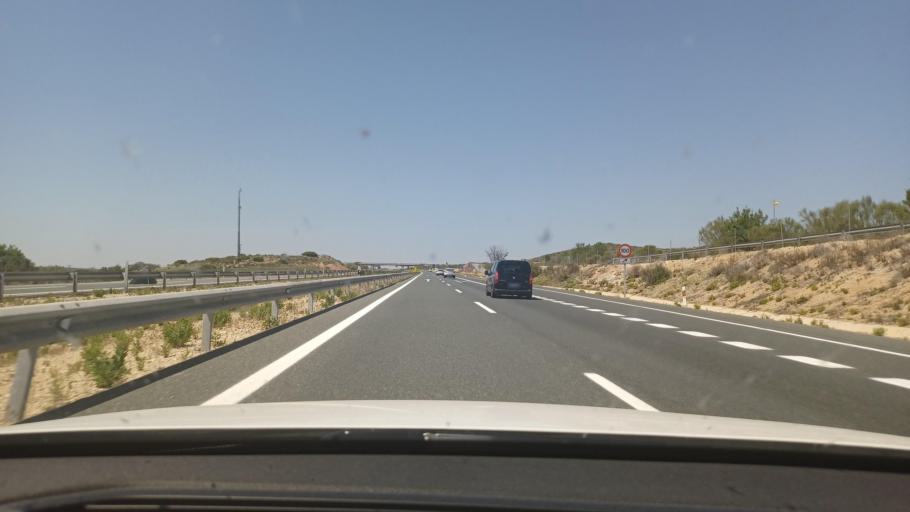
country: ES
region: Castille-La Mancha
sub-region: Provincia de Albacete
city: Almansa
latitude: 38.8791
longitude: -1.1662
